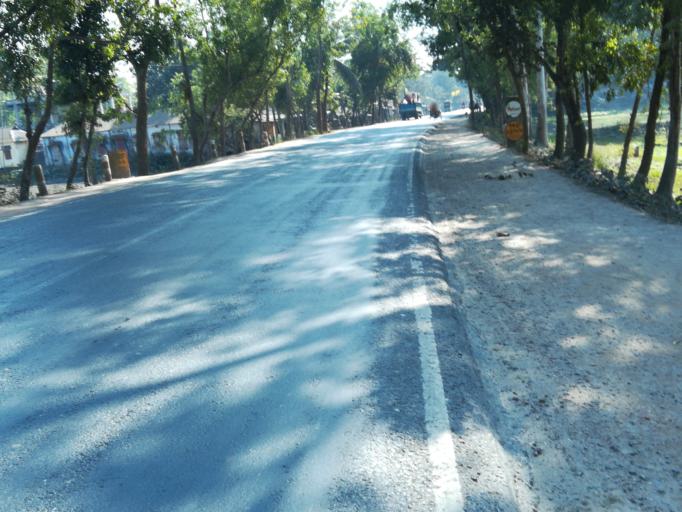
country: BD
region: Rangpur Division
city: Rangpur
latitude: 25.5753
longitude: 89.2745
